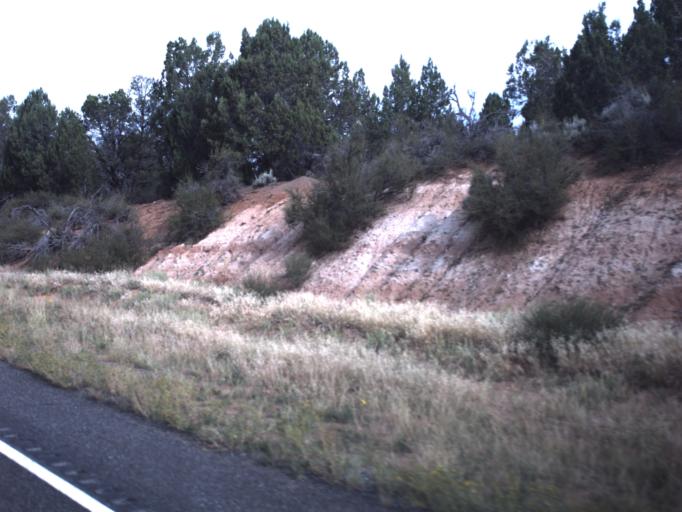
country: US
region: Utah
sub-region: Kane County
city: Kanab
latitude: 37.2231
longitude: -112.7166
